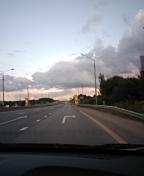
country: RU
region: Moskovskaya
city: Zhukovskiy
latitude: 55.5108
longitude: 38.1344
